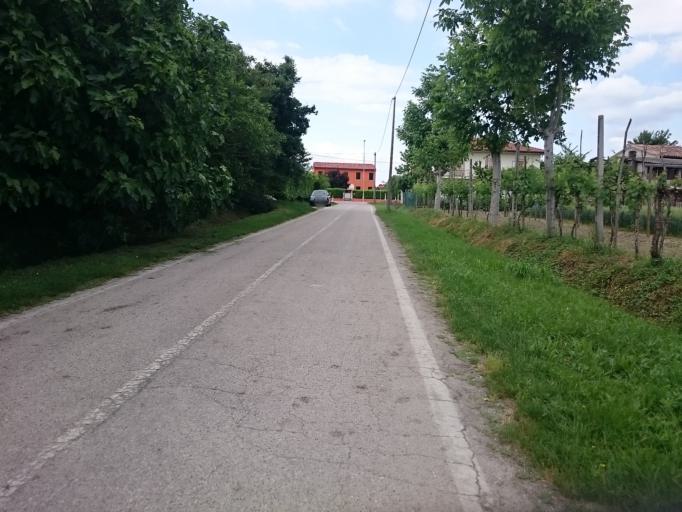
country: IT
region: Veneto
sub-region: Provincia di Padova
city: Ponso
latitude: 45.1993
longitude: 11.5738
